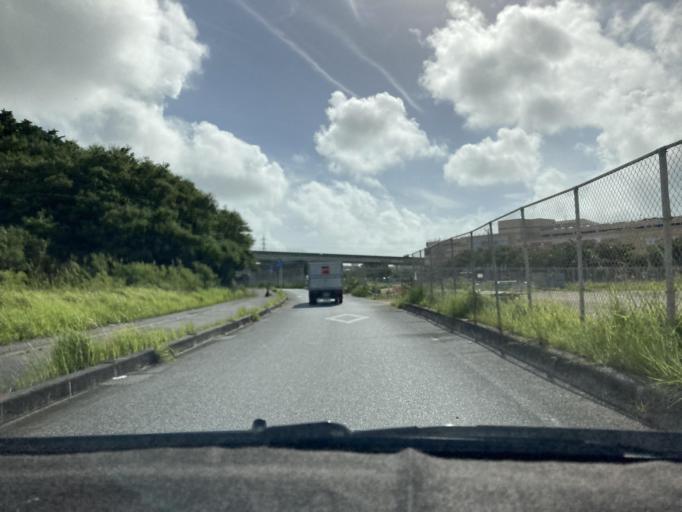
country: JP
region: Okinawa
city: Naha-shi
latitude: 26.2027
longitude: 127.7365
